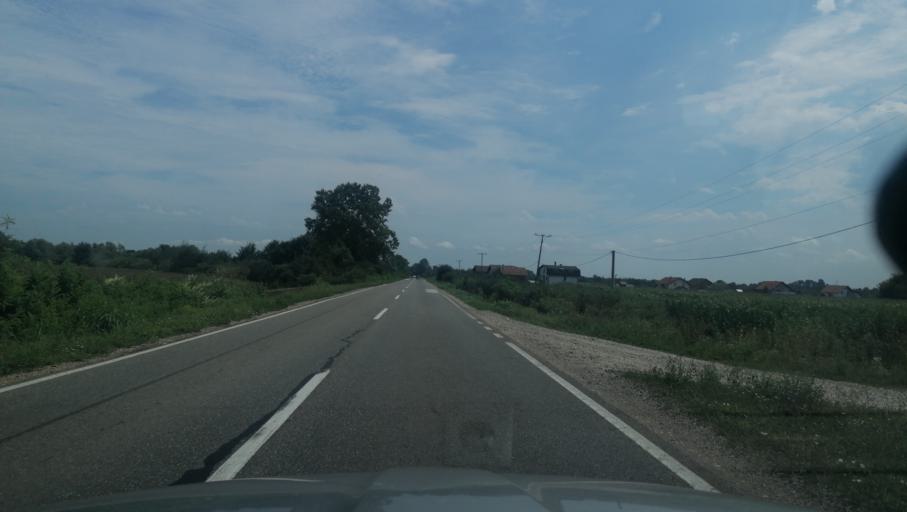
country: BA
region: Republika Srpska
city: Bosanski Samac
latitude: 45.0408
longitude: 18.4964
